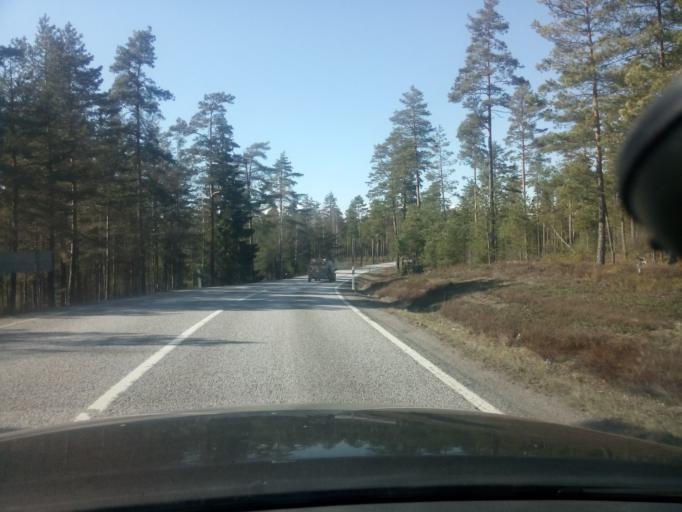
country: SE
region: Soedermanland
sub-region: Nykopings Kommun
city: Stigtomta
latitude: 58.8914
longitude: 16.8320
